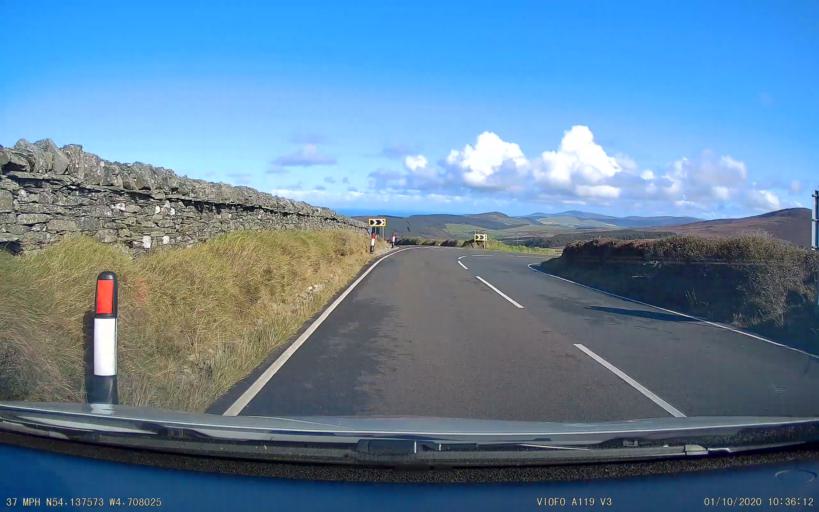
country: IM
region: Port Erin
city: Port Erin
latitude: 54.1375
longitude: -4.7081
